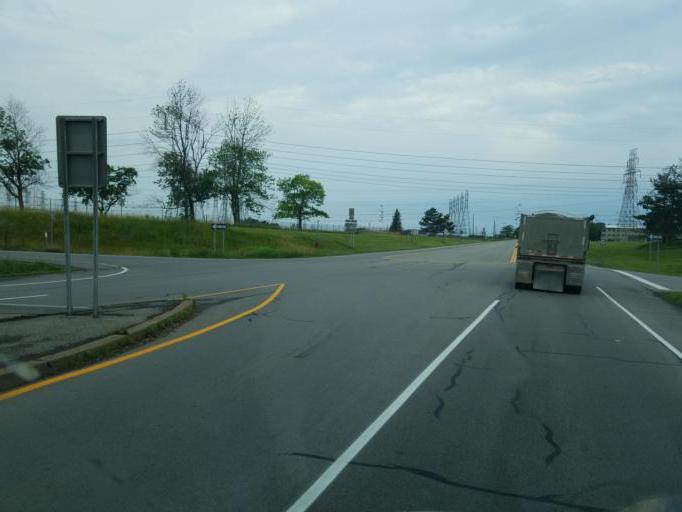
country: US
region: New York
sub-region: Niagara County
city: Lewiston
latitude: 43.1303
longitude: -79.0189
